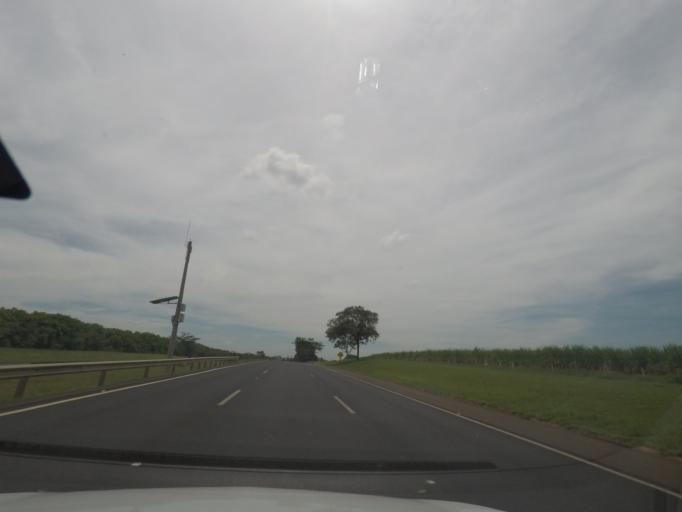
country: BR
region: Sao Paulo
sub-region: Bebedouro
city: Bebedouro
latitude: -20.9888
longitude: -48.4342
